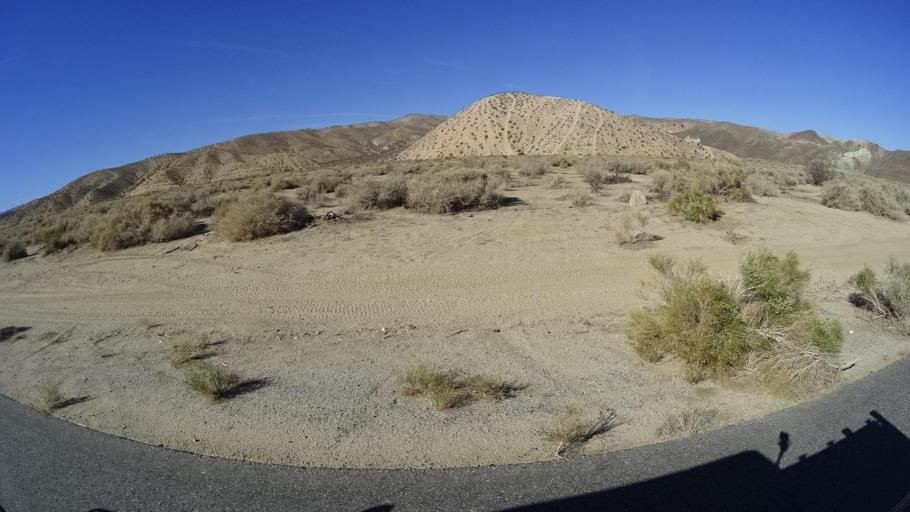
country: US
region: California
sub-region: Kern County
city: California City
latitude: 35.3122
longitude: -118.0912
